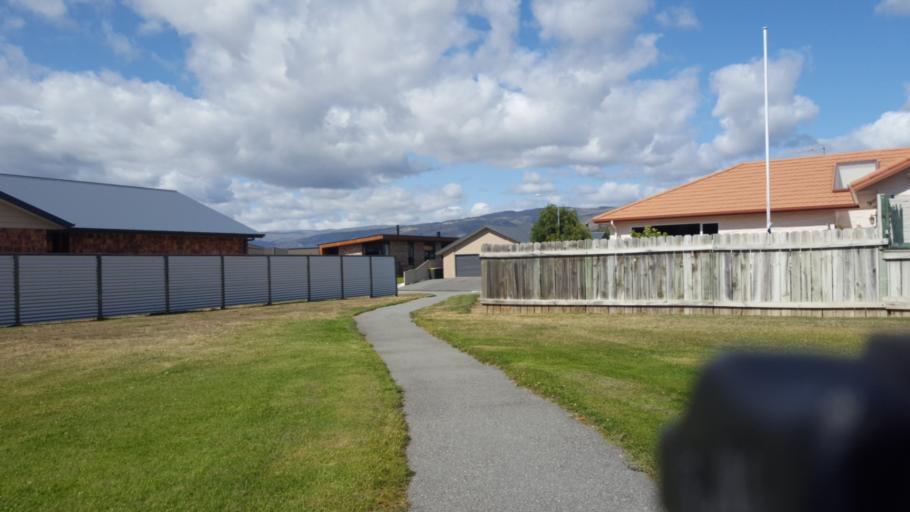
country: NZ
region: Otago
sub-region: Queenstown-Lakes District
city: Wanaka
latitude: -45.0428
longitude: 169.1822
